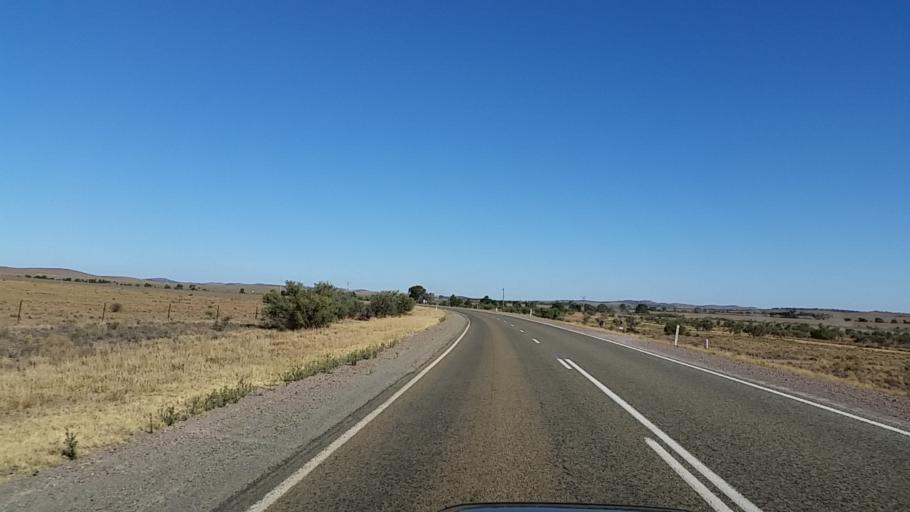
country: AU
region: South Australia
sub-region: Flinders Ranges
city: Quorn
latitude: -32.4295
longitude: 138.5315
